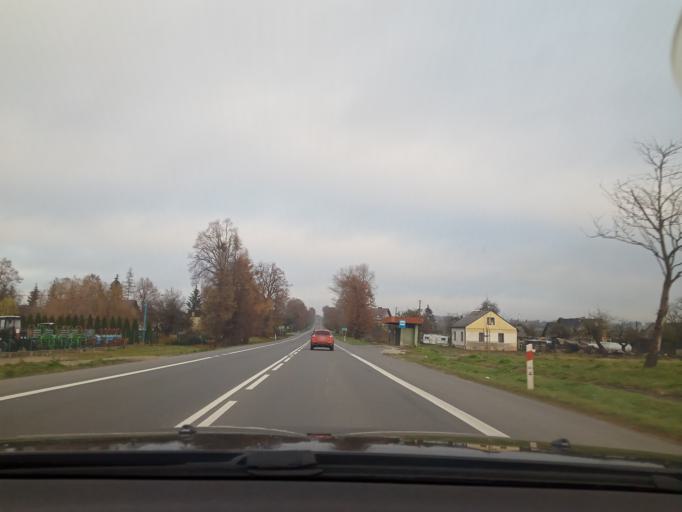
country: PL
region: Lesser Poland Voivodeship
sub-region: Powiat miechowski
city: Miechow
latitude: 50.3355
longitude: 20.0342
